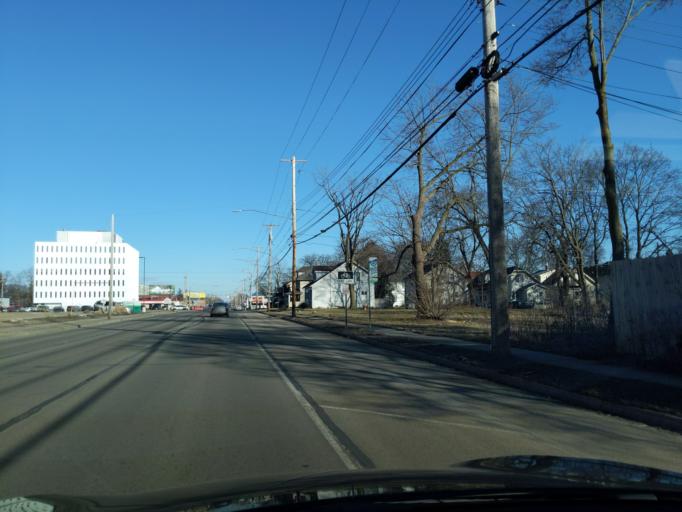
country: US
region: Michigan
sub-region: Ingham County
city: Lansing
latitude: 42.7410
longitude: -84.5701
